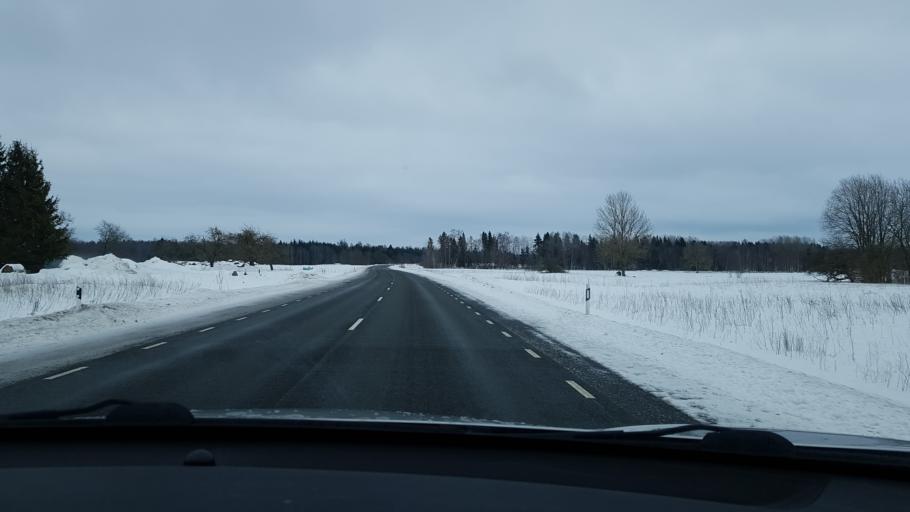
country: EE
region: Jaervamaa
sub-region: Jaerva-Jaani vald
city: Jarva-Jaani
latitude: 59.0818
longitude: 25.8426
